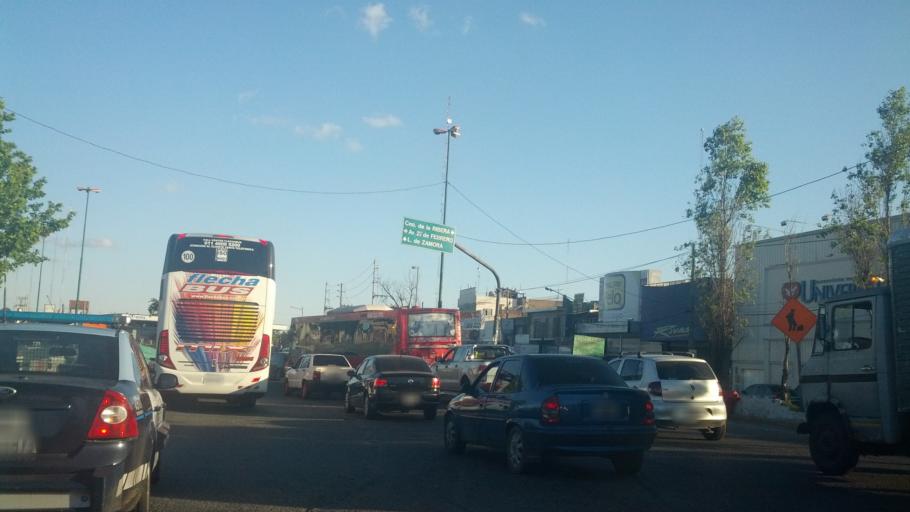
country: AR
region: Buenos Aires F.D.
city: Villa Lugano
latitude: -34.7068
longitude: -58.4593
